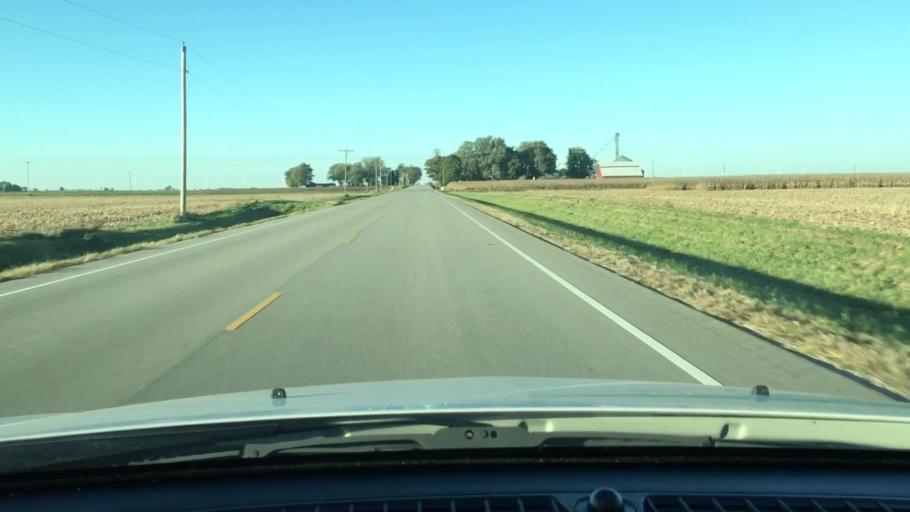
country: US
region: Illinois
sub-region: DeKalb County
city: Malta
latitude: 41.8172
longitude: -88.8864
